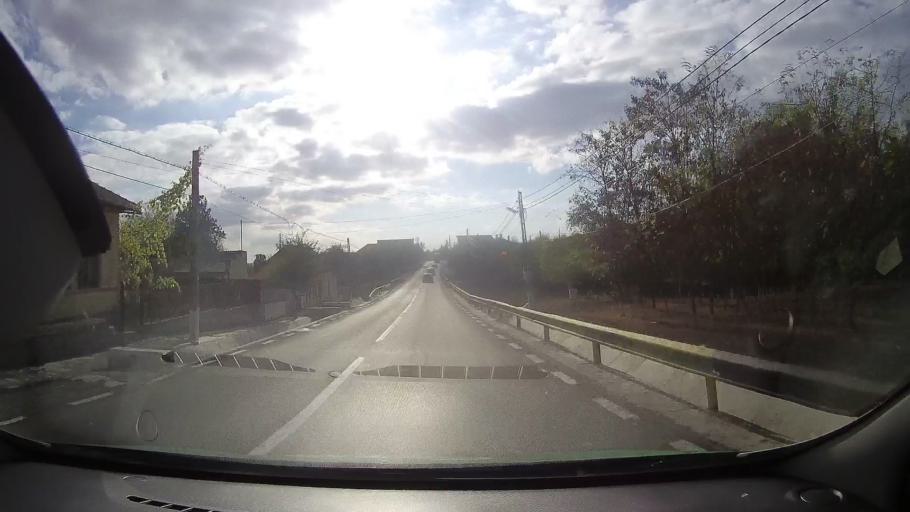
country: RO
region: Tulcea
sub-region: Comuna Topolog
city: Topolog
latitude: 44.8818
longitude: 28.3783
